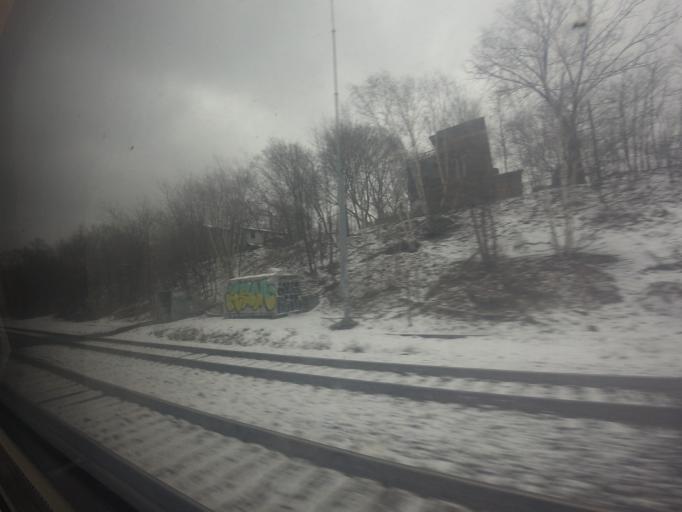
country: CA
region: Ontario
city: Scarborough
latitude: 43.6829
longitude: -79.3092
